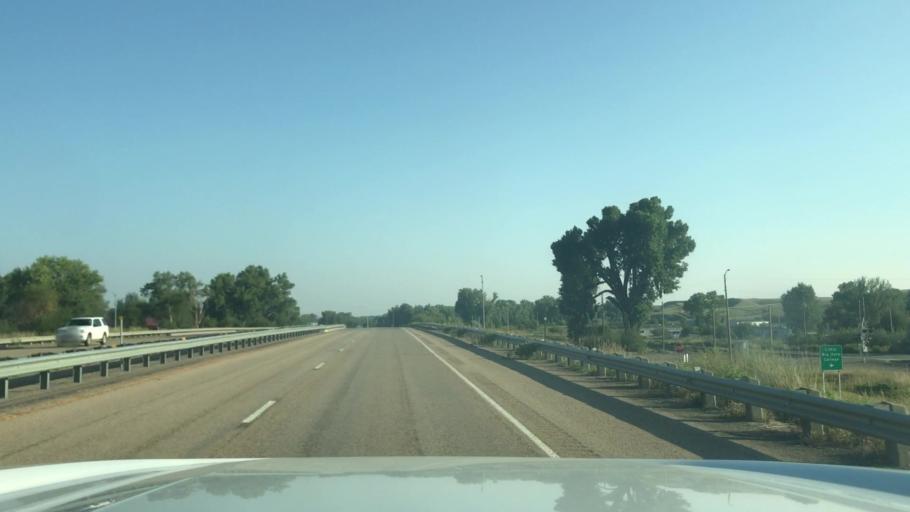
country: US
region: Montana
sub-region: Big Horn County
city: Crow Agency
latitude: 45.6023
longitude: -107.4632
